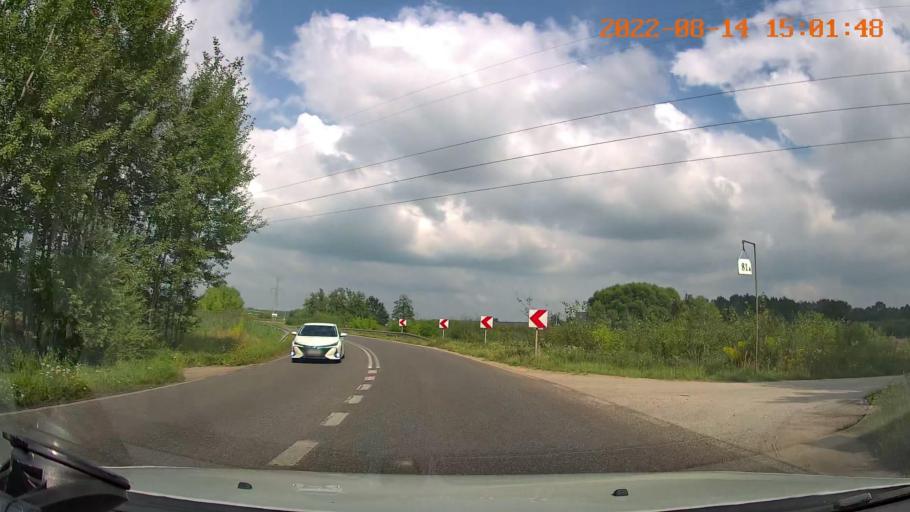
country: PL
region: Swietokrzyskie
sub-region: Powiat kielecki
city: Piekoszow
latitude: 50.8812
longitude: 20.5146
